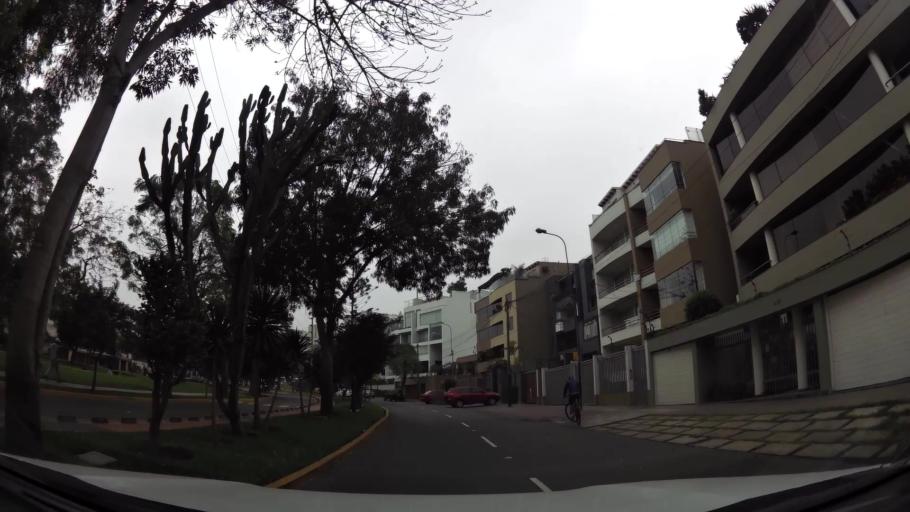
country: PE
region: Lima
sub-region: Lima
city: Surco
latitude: -12.1152
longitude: -76.9792
